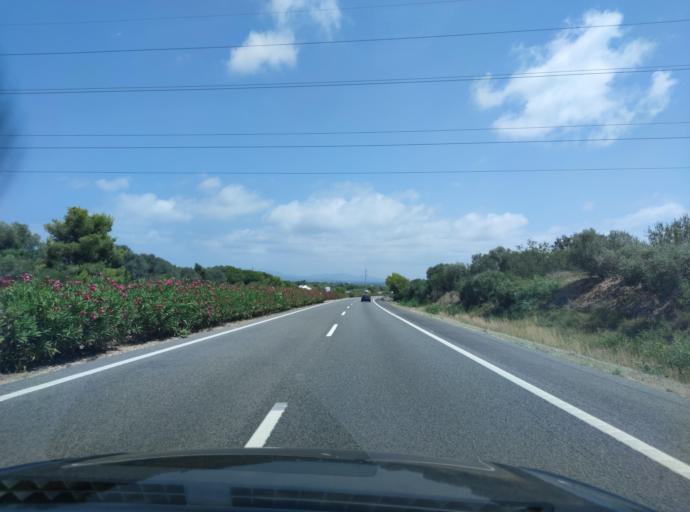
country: ES
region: Catalonia
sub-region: Provincia de Tarragona
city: Masdenverge
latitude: 40.7108
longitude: 0.5543
